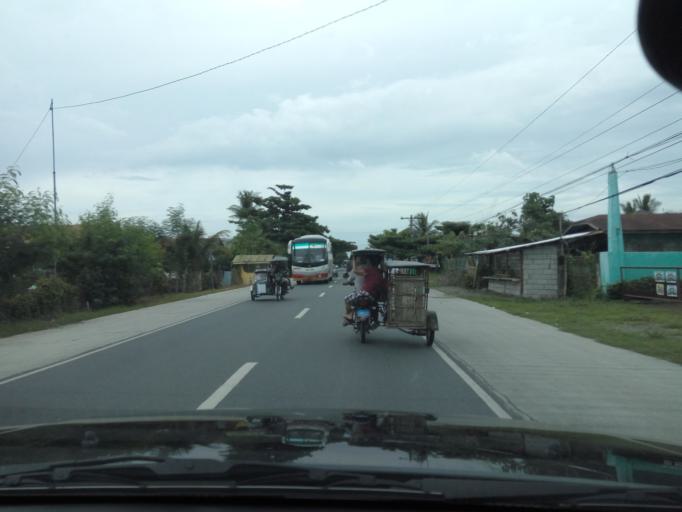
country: PH
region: Central Luzon
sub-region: Province of Nueva Ecija
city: Concepcion
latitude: 15.4479
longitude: 120.8106
